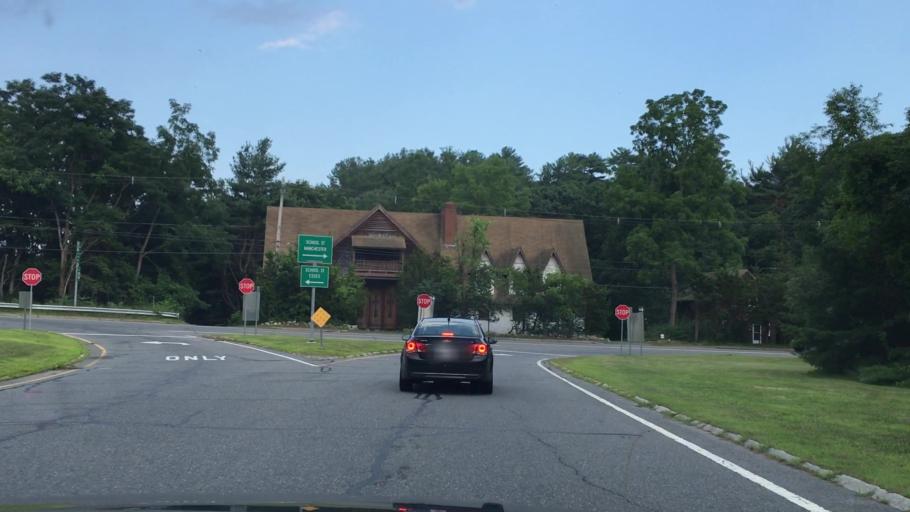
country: US
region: Massachusetts
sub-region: Essex County
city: Essex
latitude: 42.5889
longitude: -70.7665
